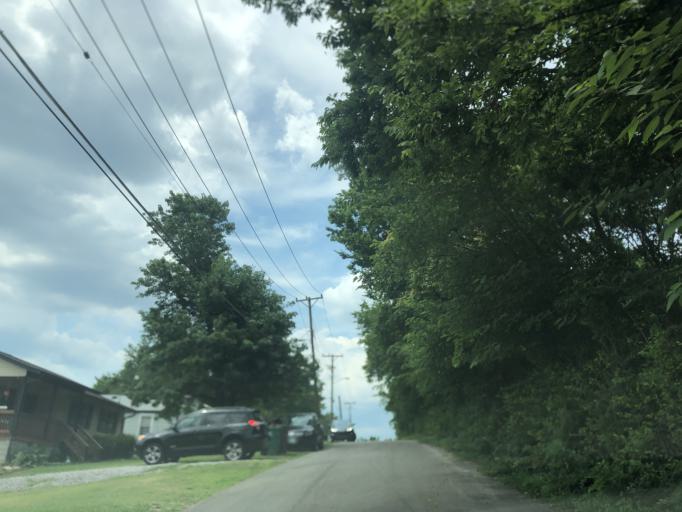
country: US
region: Tennessee
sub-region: Davidson County
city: Nashville
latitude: 36.1386
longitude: -86.7560
